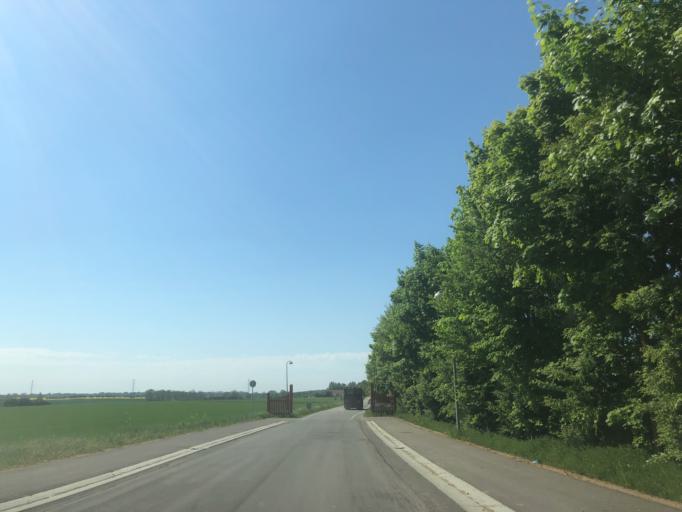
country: DK
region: Capital Region
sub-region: Hoje-Taastrup Kommune
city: Taastrup
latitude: 55.6266
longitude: 12.2450
